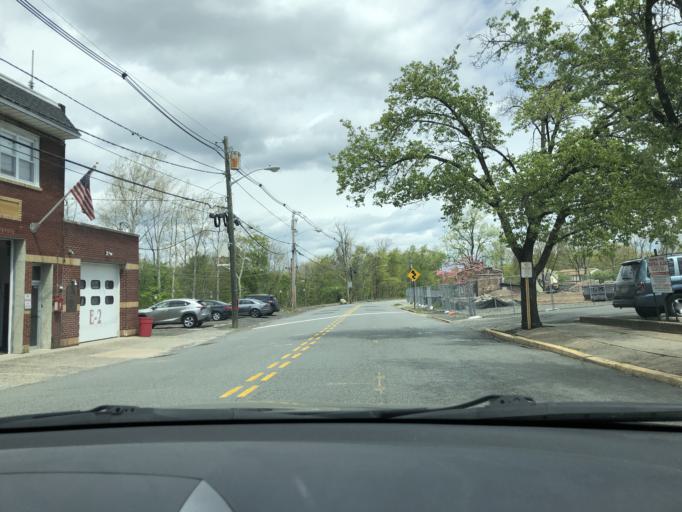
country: US
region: New Jersey
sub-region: Passaic County
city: Singac
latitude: 40.8817
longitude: -74.2269
